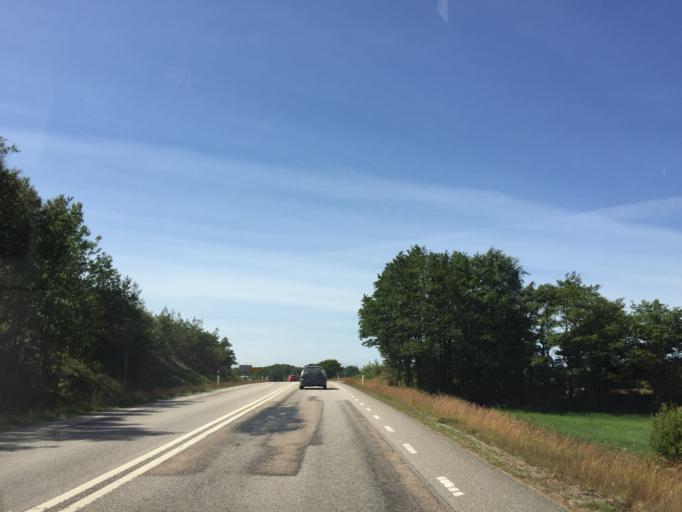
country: SE
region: Vaestra Goetaland
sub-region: Lysekils Kommun
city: Lysekil
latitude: 58.3055
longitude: 11.4819
